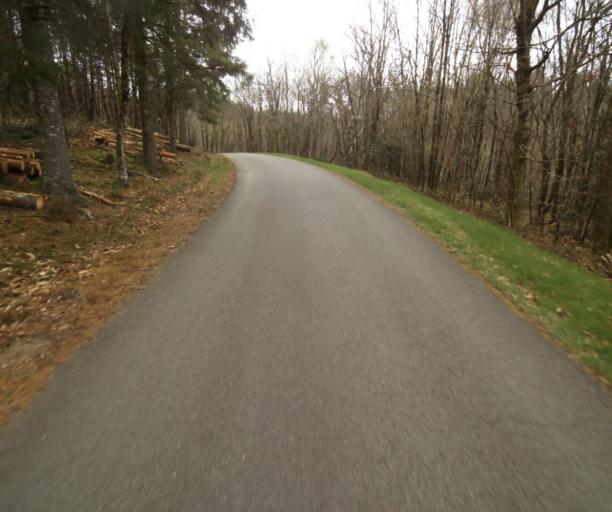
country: FR
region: Limousin
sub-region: Departement de la Correze
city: Correze
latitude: 45.3237
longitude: 1.9417
